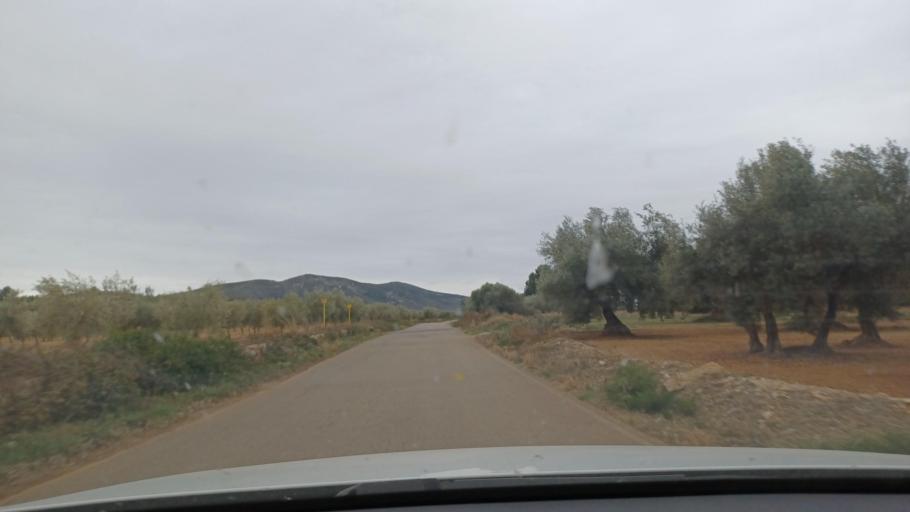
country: ES
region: Valencia
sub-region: Provincia de Castello
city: Canet lo Roig
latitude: 40.5690
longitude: 0.2754
